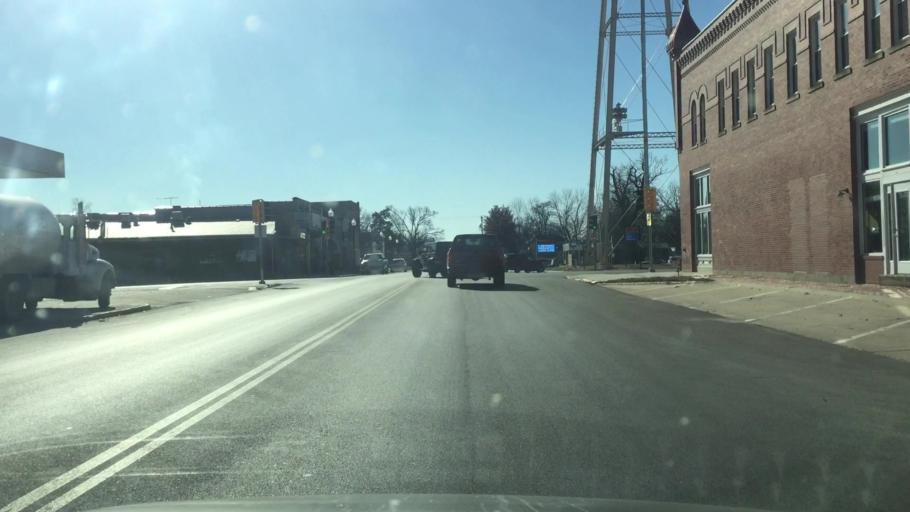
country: US
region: Kansas
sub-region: Allen County
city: Humboldt
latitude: 37.8117
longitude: -95.4355
